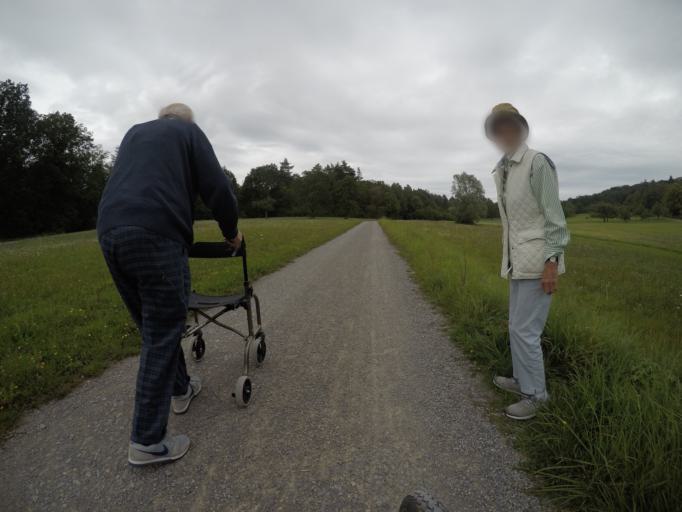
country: DE
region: Baden-Wuerttemberg
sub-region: Regierungsbezirk Stuttgart
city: Nufringen
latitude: 48.6063
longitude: 8.8866
